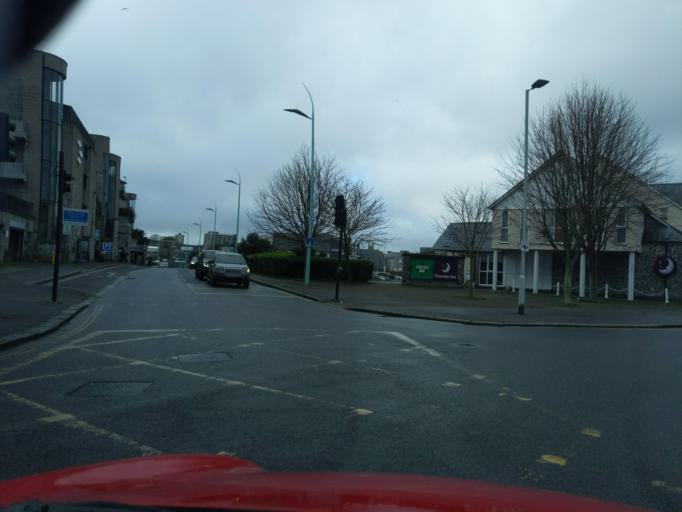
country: GB
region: England
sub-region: Plymouth
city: Plymouth
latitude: 50.3675
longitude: -4.1275
